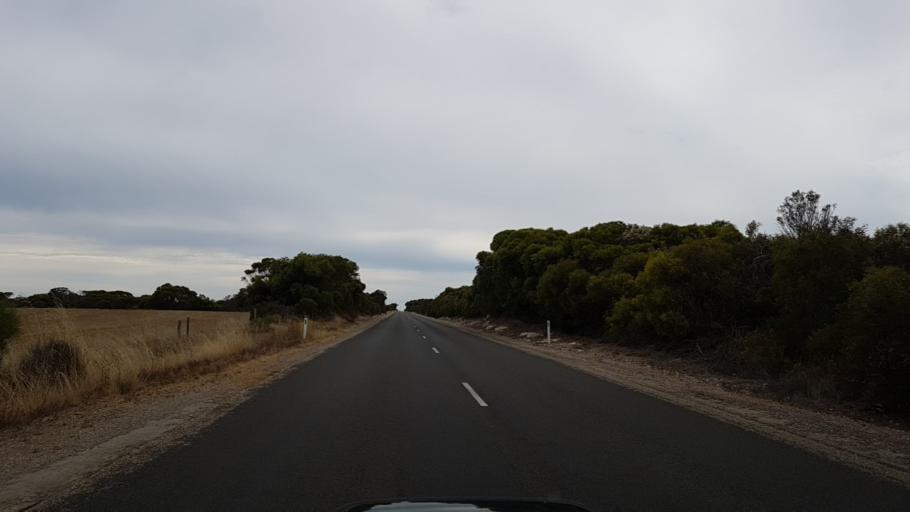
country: AU
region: South Australia
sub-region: Yorke Peninsula
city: Honiton
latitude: -34.9879
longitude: 137.1402
